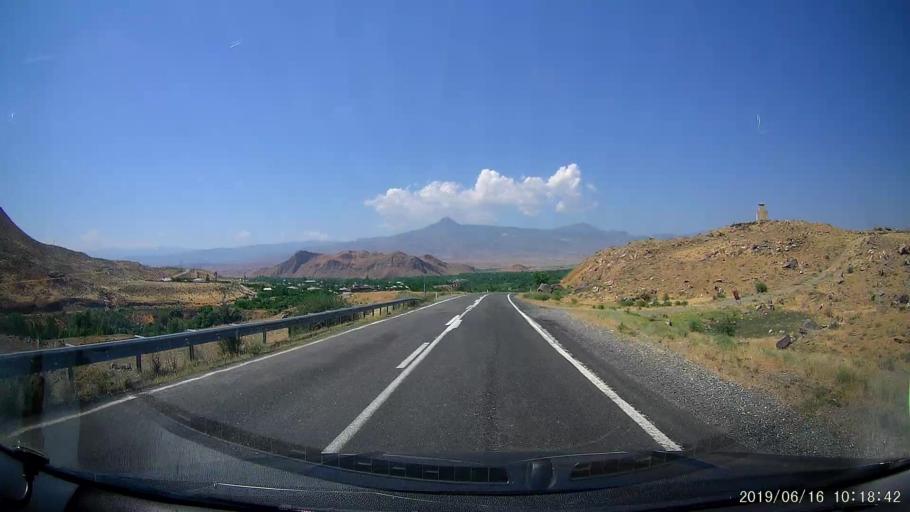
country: TR
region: Igdir
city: Tuzluca
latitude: 40.1579
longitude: 43.6652
